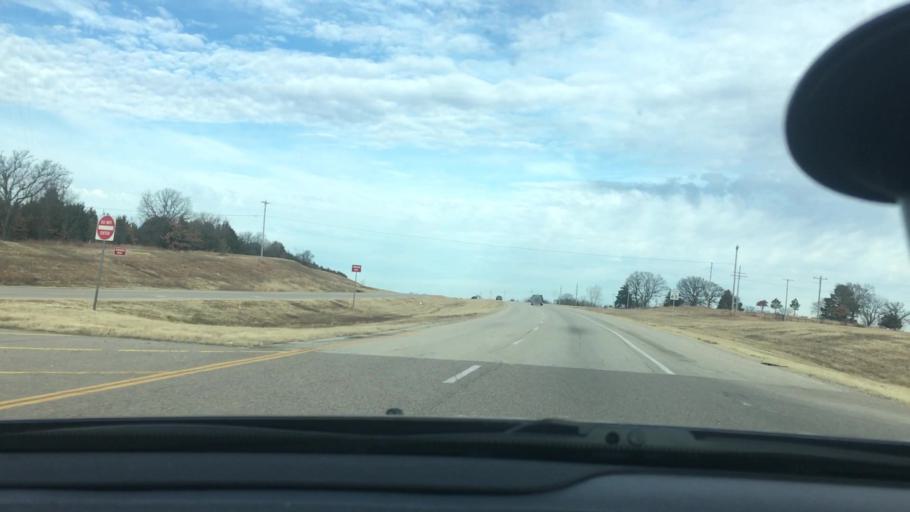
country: US
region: Oklahoma
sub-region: Pontotoc County
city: Byng
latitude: 34.8997
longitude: -96.6748
